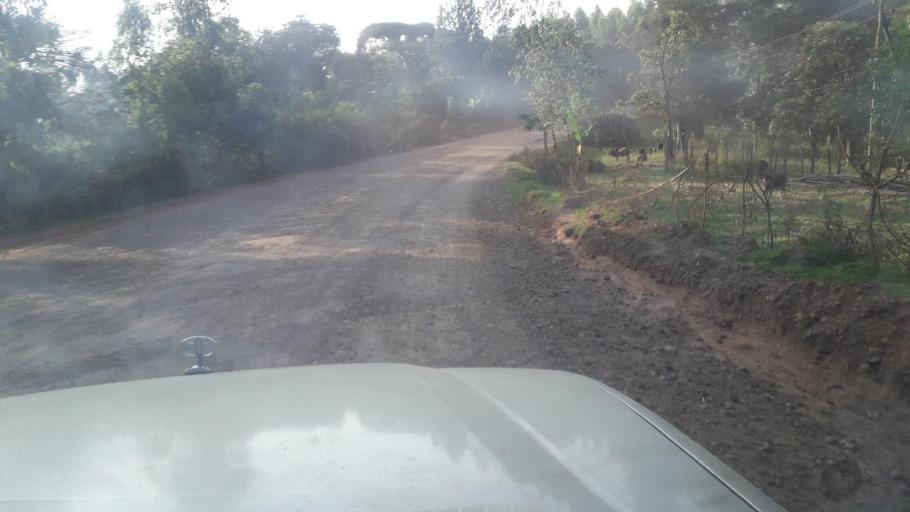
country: ET
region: Oromiya
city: Jima
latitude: 7.6020
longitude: 36.8428
